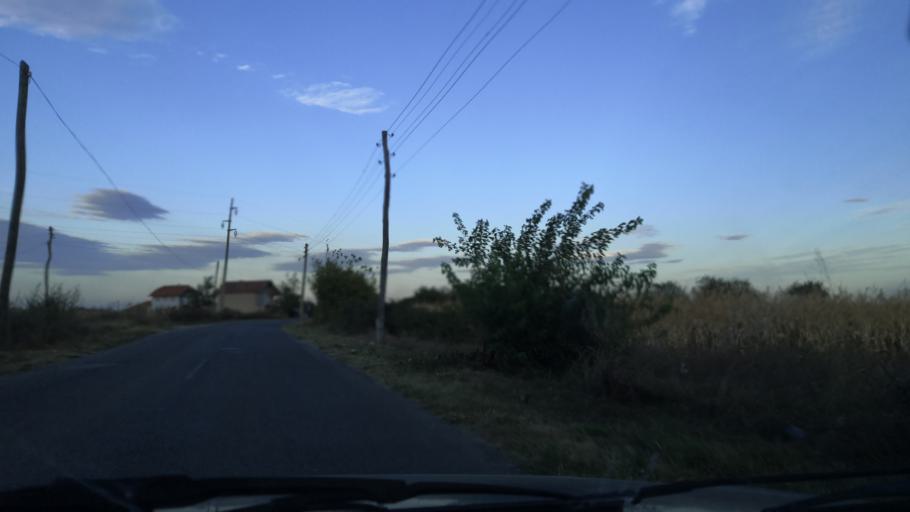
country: RS
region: Central Serbia
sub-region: Borski Okrug
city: Negotin
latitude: 44.2393
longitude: 22.5541
